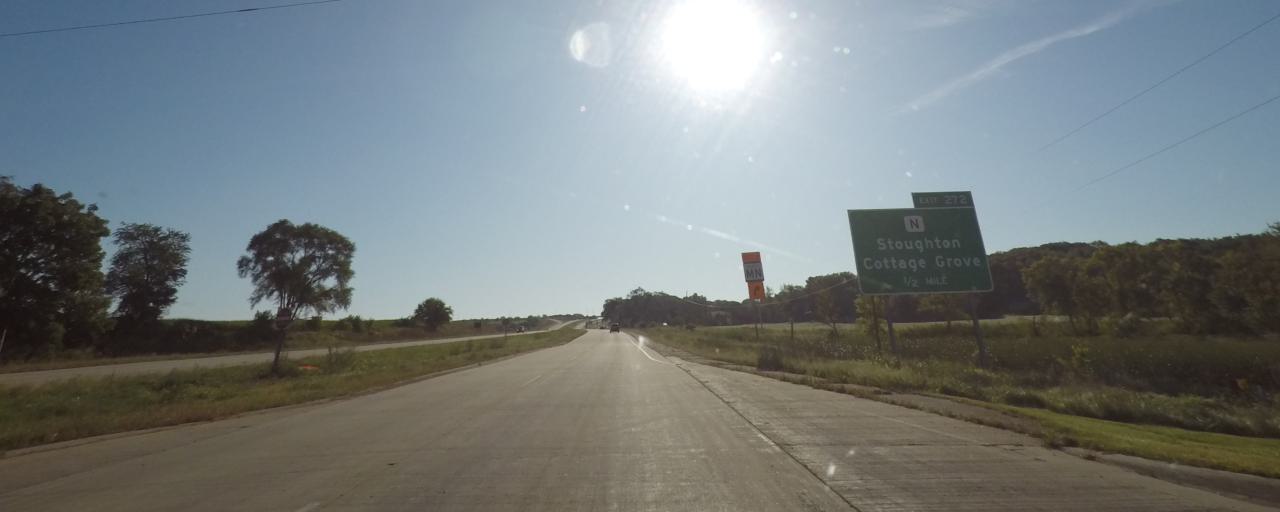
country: US
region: Wisconsin
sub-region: Dane County
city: Cottage Grove
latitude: 43.0335
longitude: -89.2161
